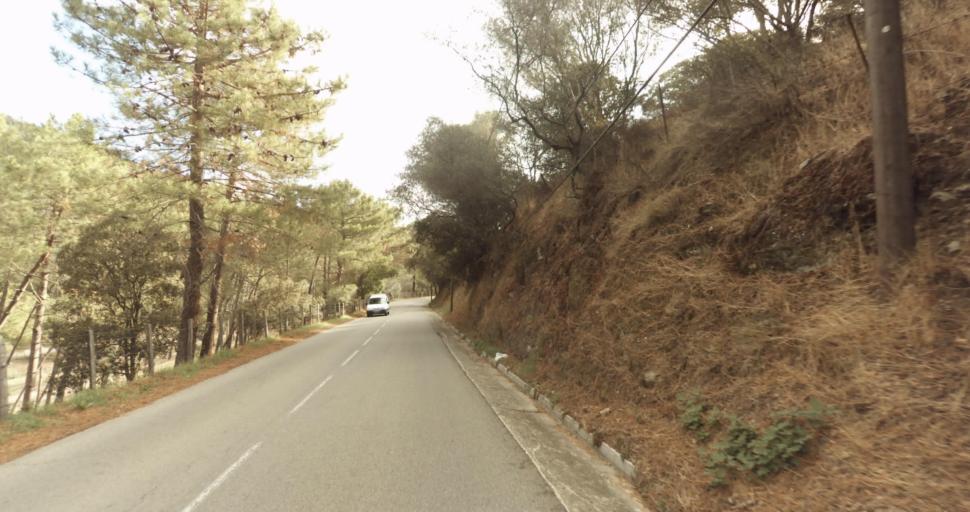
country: FR
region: Corsica
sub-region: Departement de la Corse-du-Sud
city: Ajaccio
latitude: 41.9303
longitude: 8.7082
